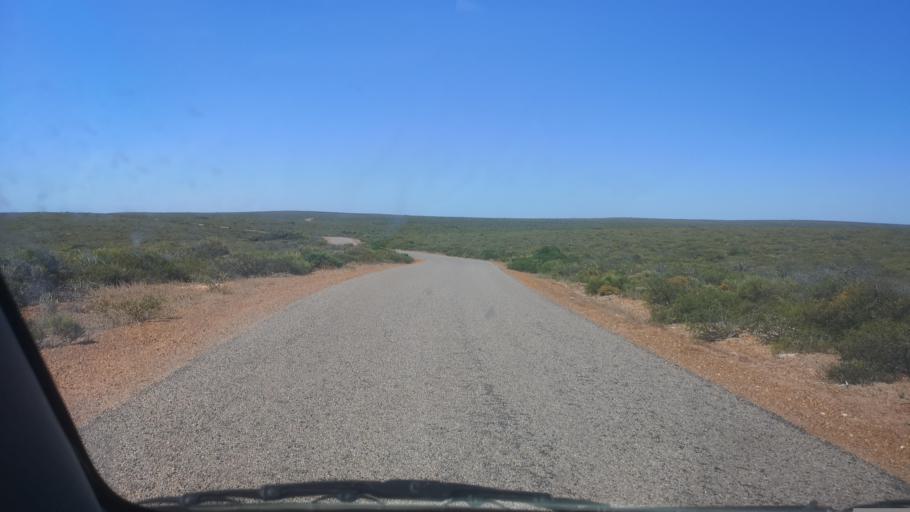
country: AU
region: Western Australia
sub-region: Northampton Shire
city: Kalbarri
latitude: -27.8167
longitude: 114.1178
